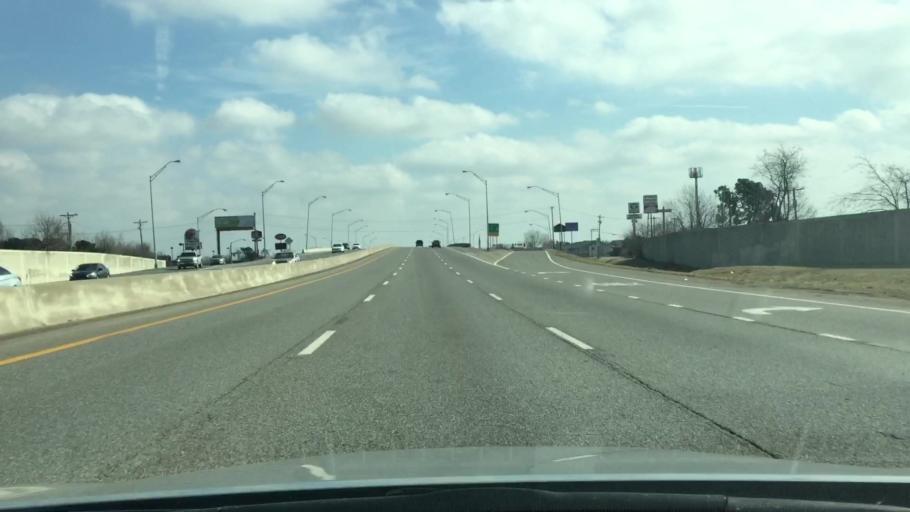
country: US
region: Oklahoma
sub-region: Oklahoma County
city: Oklahoma City
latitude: 35.3945
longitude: -97.5686
